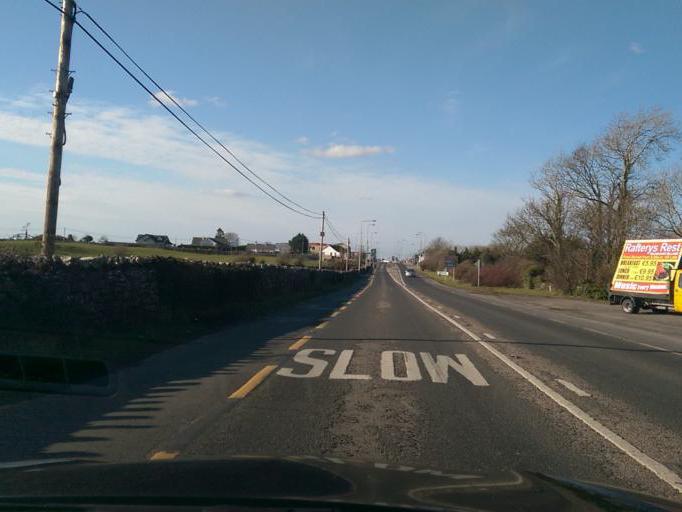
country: IE
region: Connaught
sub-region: County Galway
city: Oranmore
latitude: 53.2056
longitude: -8.8657
